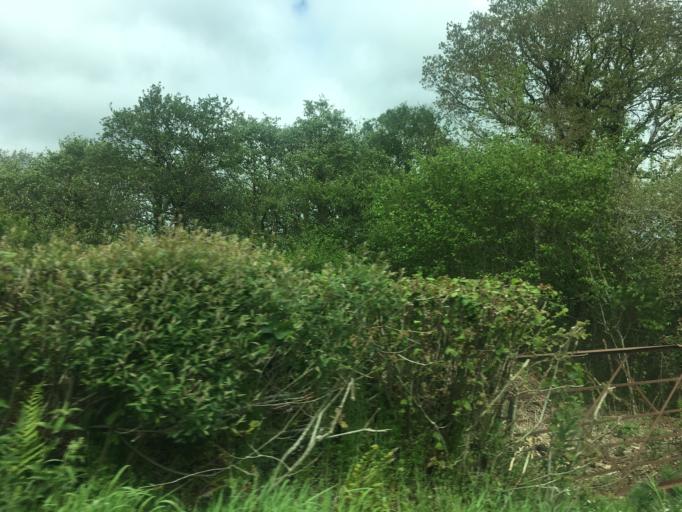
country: GB
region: Wales
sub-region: Carmarthenshire
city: Llansawel
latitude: 52.0670
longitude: -3.9800
